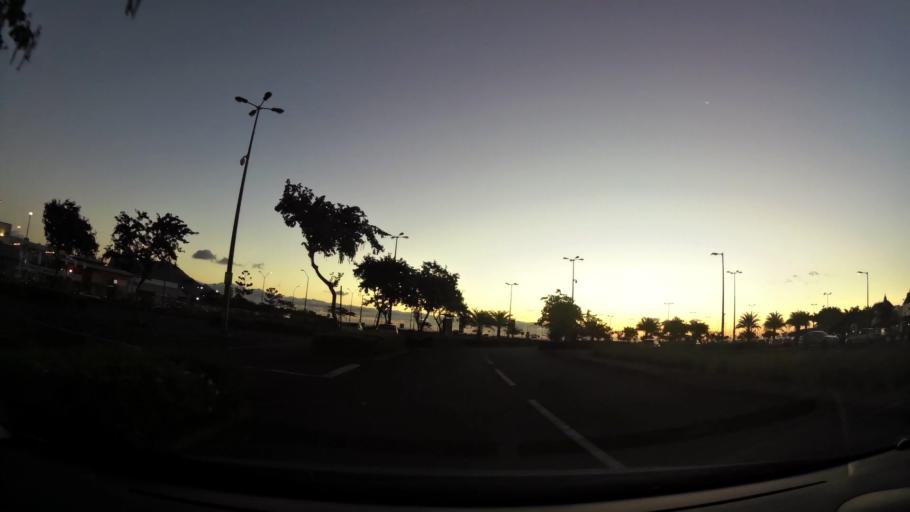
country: MU
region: Moka
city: Moka
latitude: -20.2266
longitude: 57.4976
